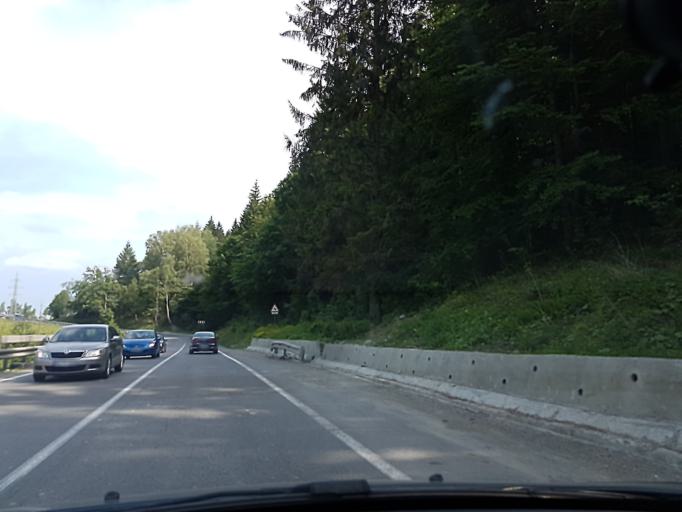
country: RO
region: Prahova
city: Maneciu
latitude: 45.3418
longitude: 25.9536
